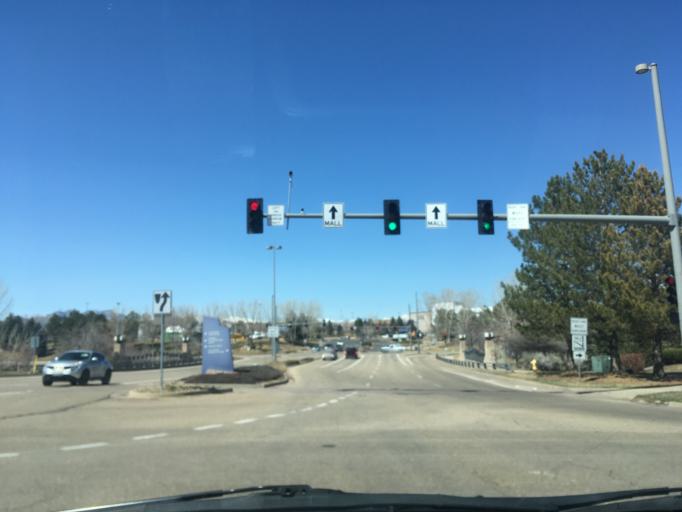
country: US
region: Colorado
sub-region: Broomfield County
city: Broomfield
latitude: 39.9291
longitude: -105.1296
